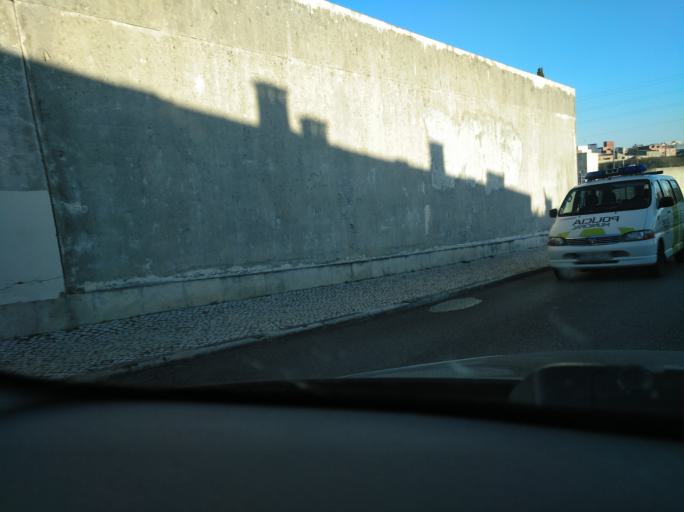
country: PT
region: Lisbon
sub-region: Odivelas
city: Pontinha
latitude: 38.7718
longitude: -9.1869
